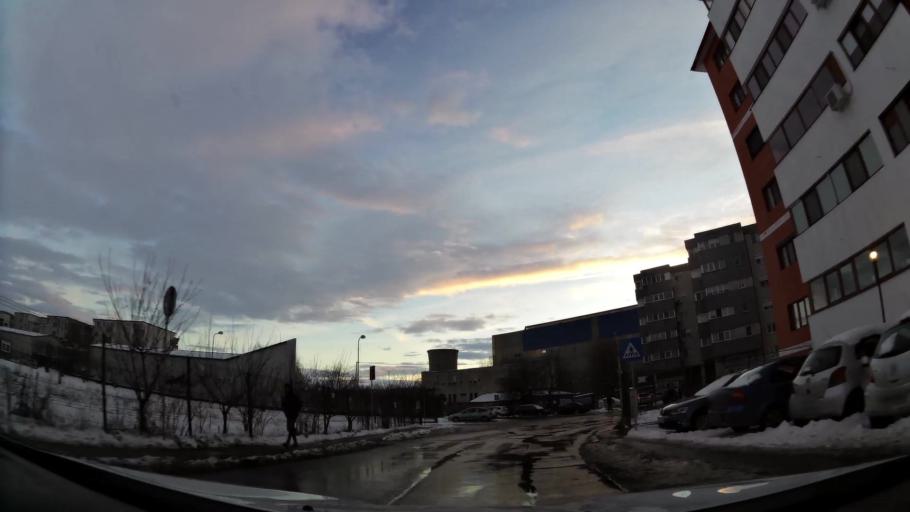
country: RO
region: Ilfov
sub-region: Comuna Popesti-Leordeni
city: Popesti-Leordeni
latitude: 44.3639
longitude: 26.1489
